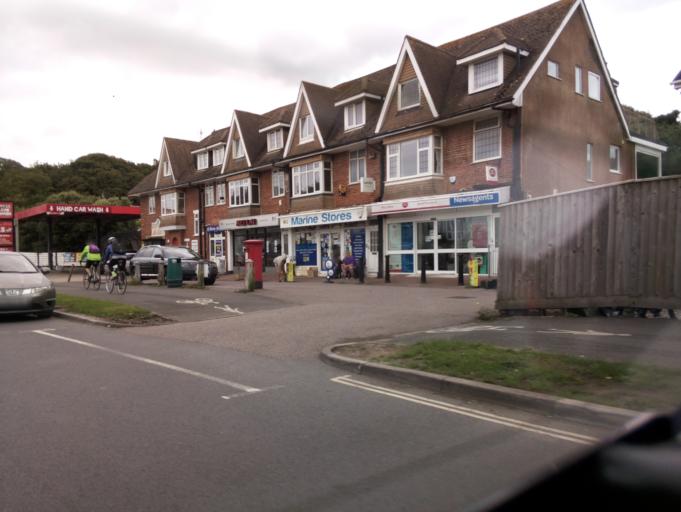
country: GB
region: England
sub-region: Devon
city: Dawlish
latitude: 50.5879
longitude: -3.4562
